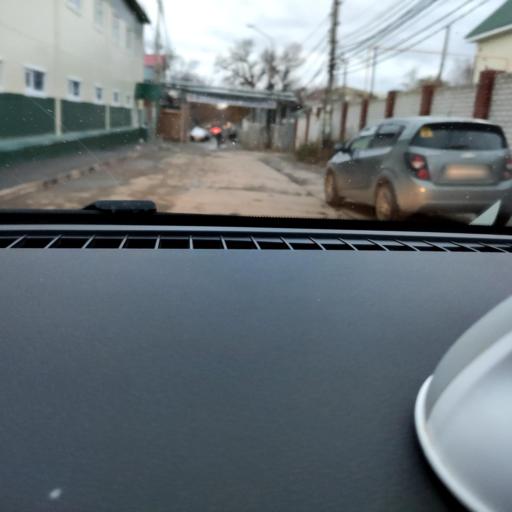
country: RU
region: Samara
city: Samara
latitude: 53.2737
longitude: 50.1937
